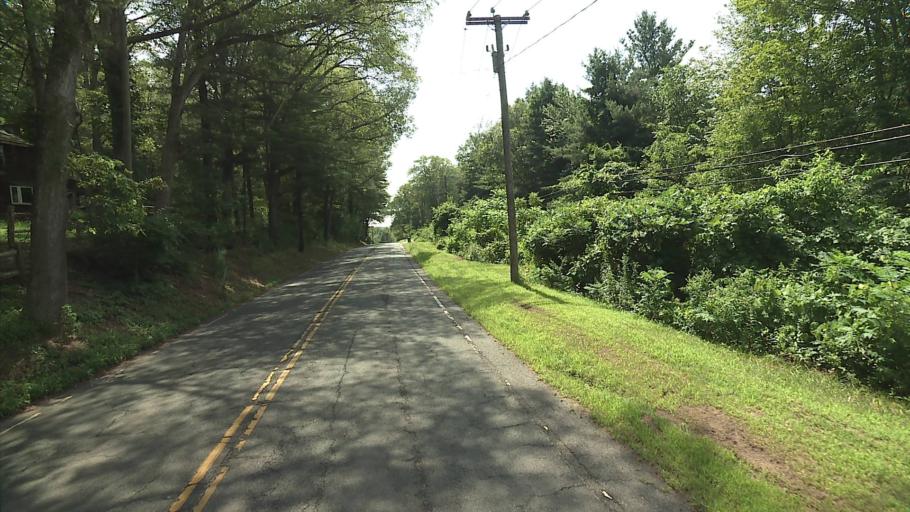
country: US
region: Connecticut
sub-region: Tolland County
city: South Coventry
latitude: 41.7615
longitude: -72.2796
